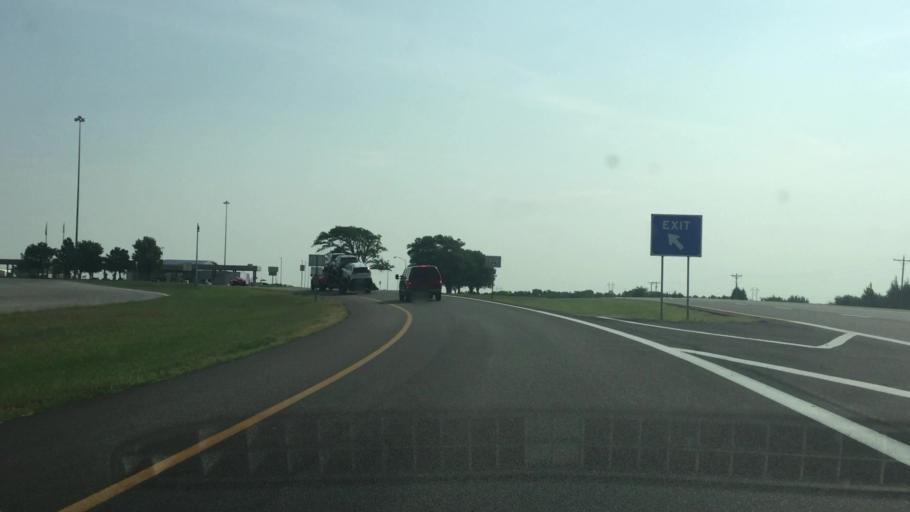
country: US
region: Kansas
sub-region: Butler County
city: Towanda
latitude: 37.7643
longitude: -96.9842
